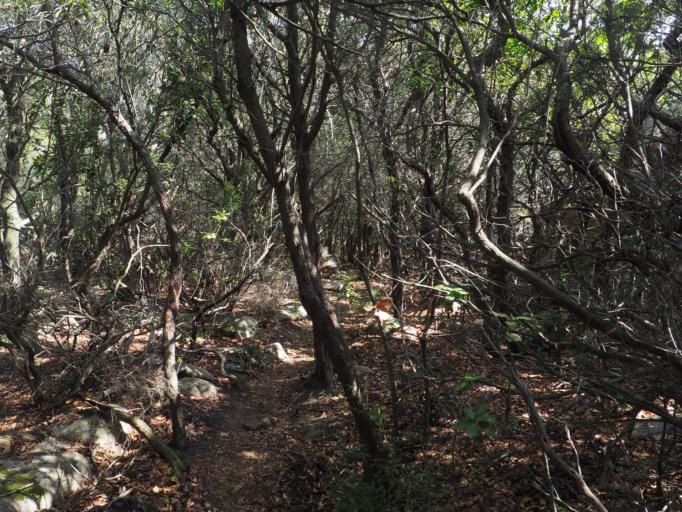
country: IT
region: Sardinia
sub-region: Provincia di Olbia-Tempio
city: Arzachena
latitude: 41.0347
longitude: 9.4766
